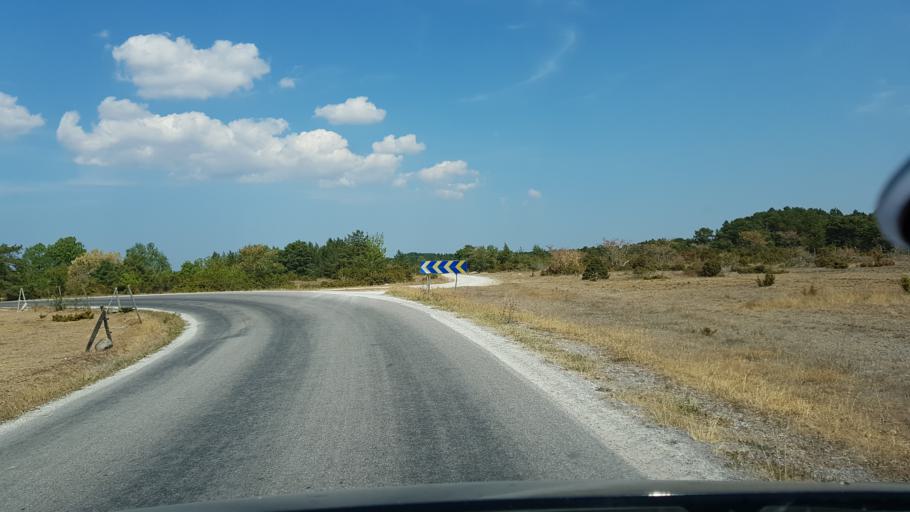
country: SE
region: Gotland
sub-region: Gotland
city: Visby
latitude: 57.6622
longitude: 18.3765
